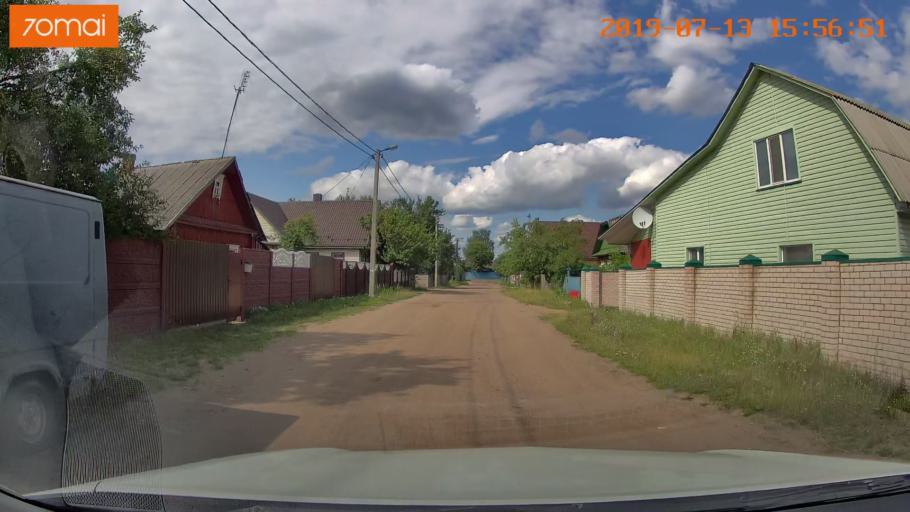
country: BY
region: Mogilev
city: Babruysk
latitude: 53.1454
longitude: 29.2024
